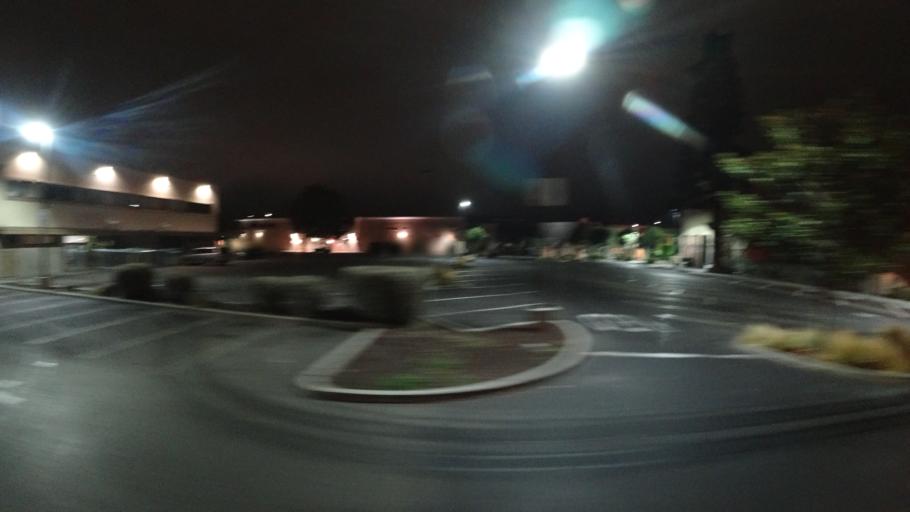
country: US
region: California
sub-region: Alameda County
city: Hayward
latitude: 37.6740
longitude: -122.0825
